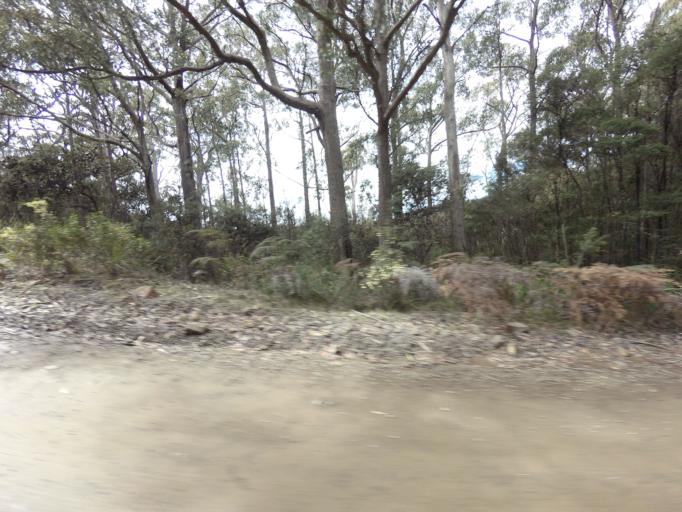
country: AU
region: Tasmania
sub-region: Huon Valley
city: Geeveston
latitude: -43.4474
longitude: 146.9051
